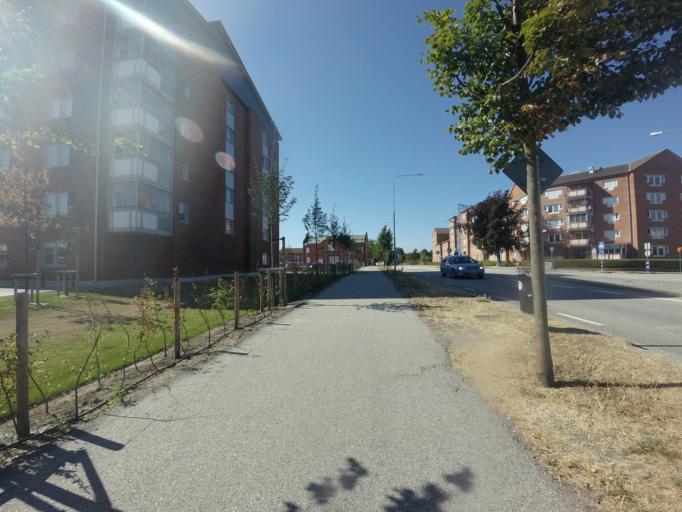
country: SE
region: Skane
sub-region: Trelleborgs Kommun
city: Trelleborg
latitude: 55.3781
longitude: 13.1493
